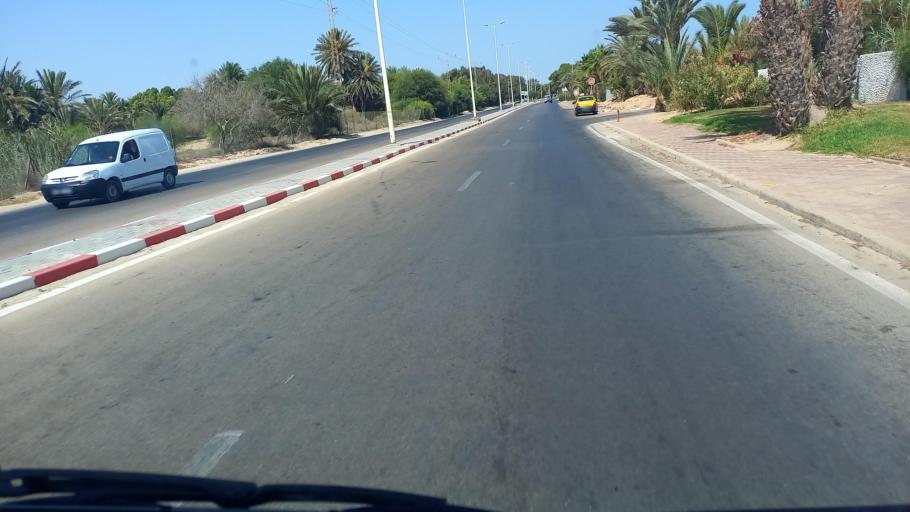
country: TN
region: Madanin
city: Midoun
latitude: 33.8258
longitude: 11.0183
